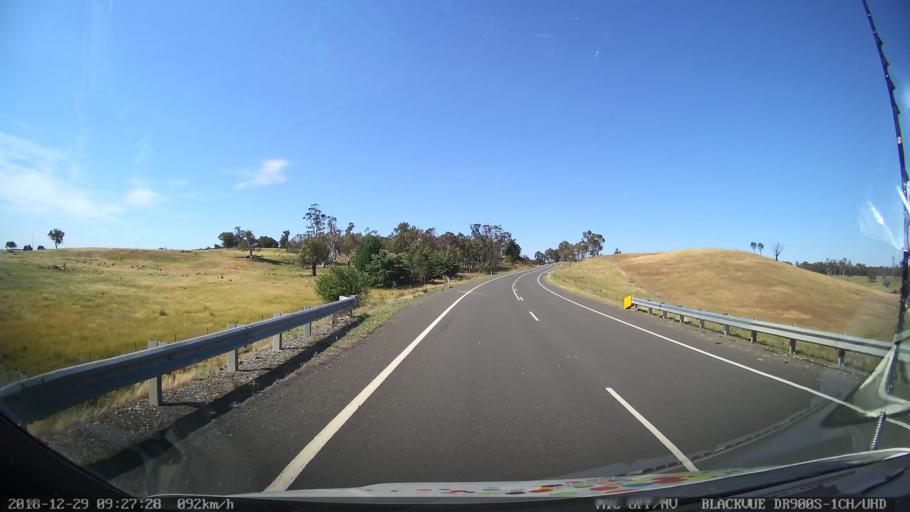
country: AU
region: New South Wales
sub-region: Upper Lachlan Shire
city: Crookwell
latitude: -34.5668
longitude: 149.3851
